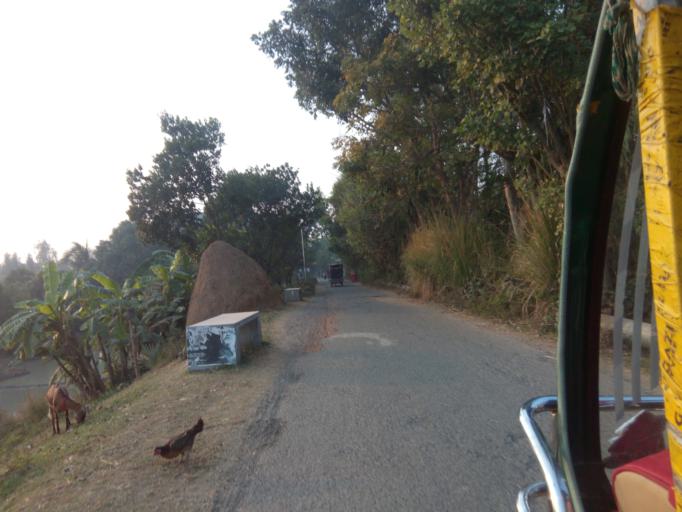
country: BD
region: Rajshahi
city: Par Naogaon
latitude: 24.4997
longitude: 89.1504
